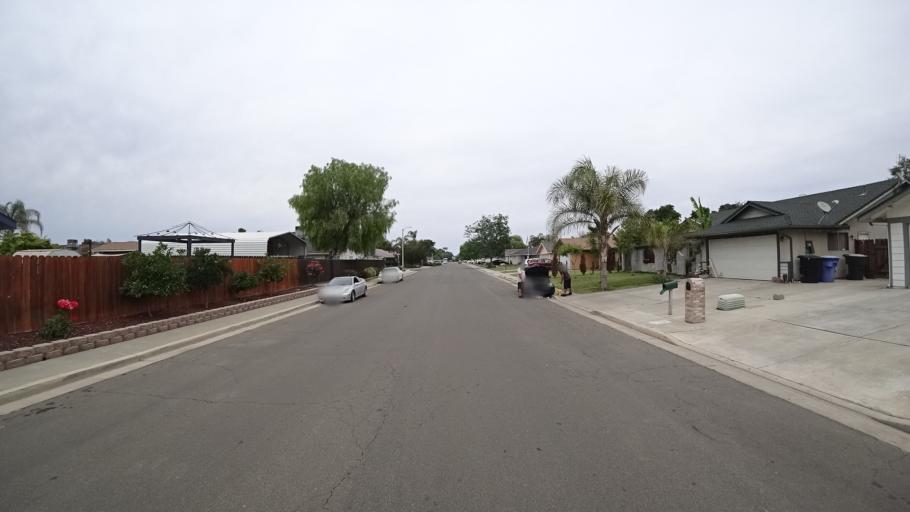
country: US
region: California
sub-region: Kings County
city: Hanford
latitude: 36.3537
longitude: -119.6325
